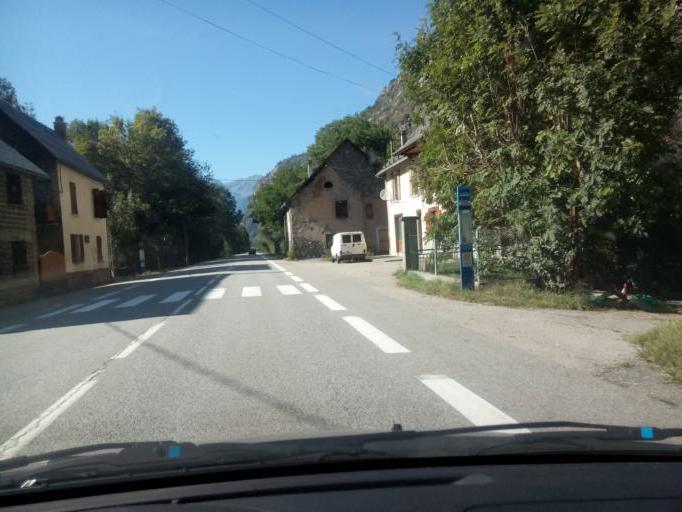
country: FR
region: Rhone-Alpes
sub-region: Departement de l'Isere
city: Huez
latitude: 45.0329
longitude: 6.0675
